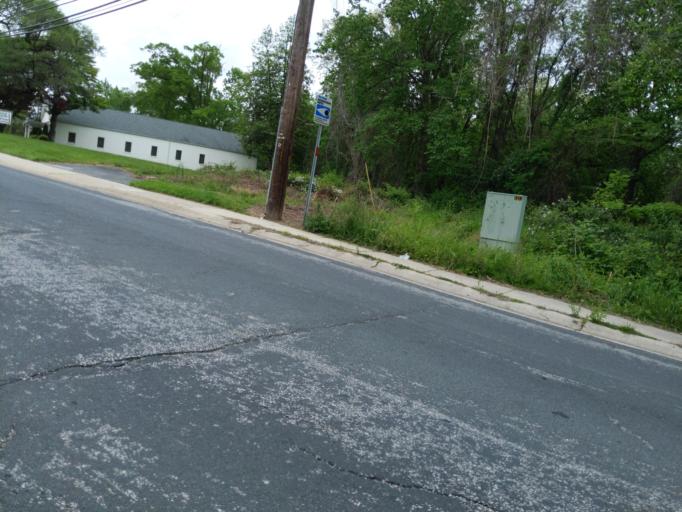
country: US
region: Maryland
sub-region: Montgomery County
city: Forest Glen
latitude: 39.0265
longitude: -77.0376
